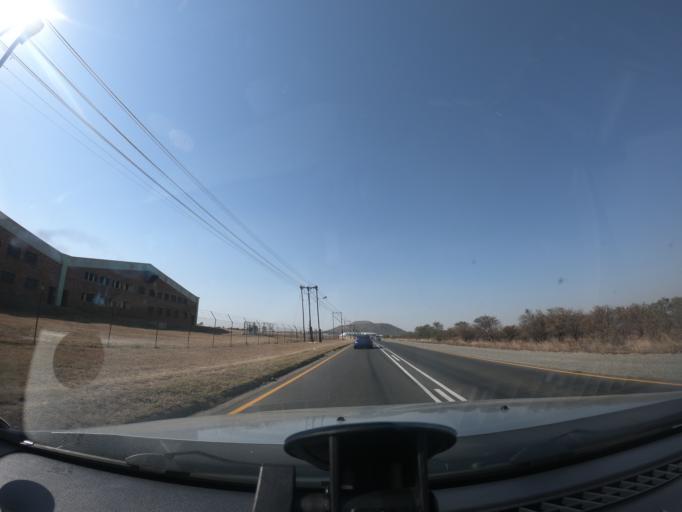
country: ZA
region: KwaZulu-Natal
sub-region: uThukela District Municipality
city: Ladysmith
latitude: -28.5460
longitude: 29.8187
